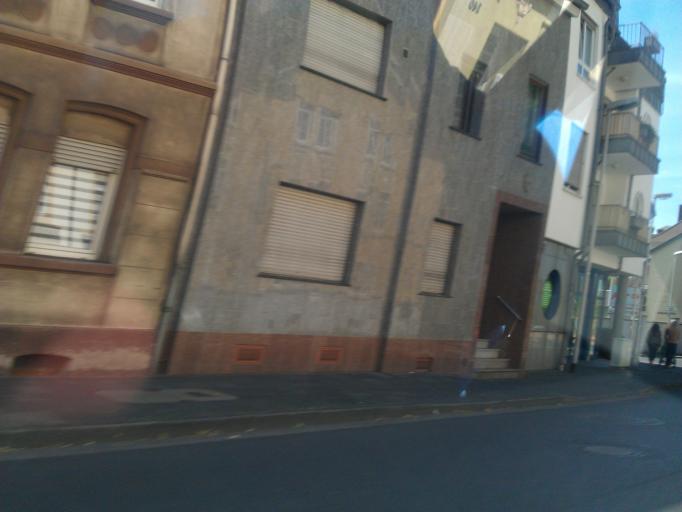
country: DE
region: North Rhine-Westphalia
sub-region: Regierungsbezirk Koln
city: Siegburg
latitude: 50.7991
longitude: 7.2016
